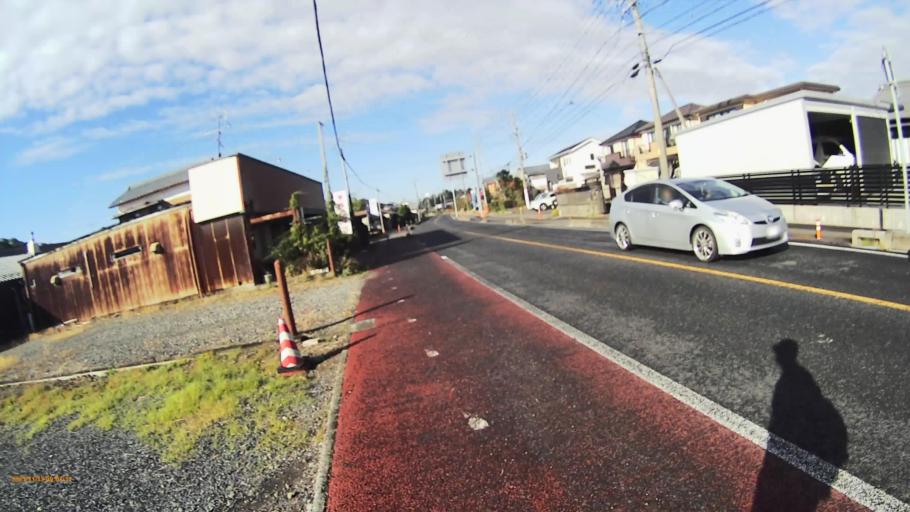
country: JP
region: Gifu
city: Mitake
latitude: 35.4381
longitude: 137.0793
